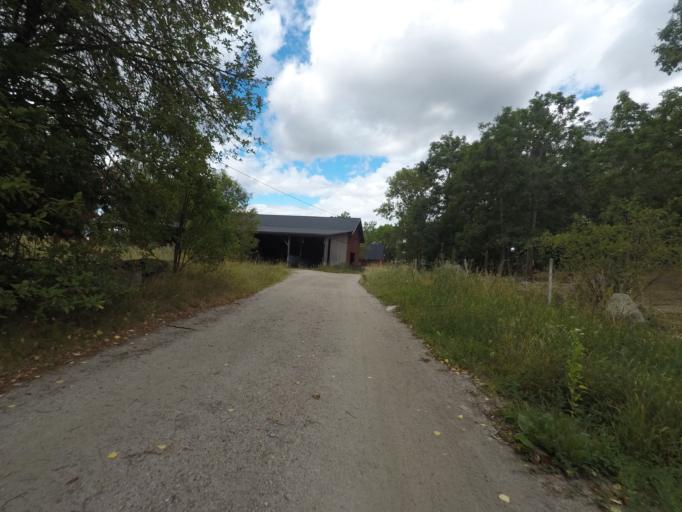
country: SE
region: Soedermanland
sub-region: Eskilstuna Kommun
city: Kvicksund
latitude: 59.4026
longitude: 16.2529
